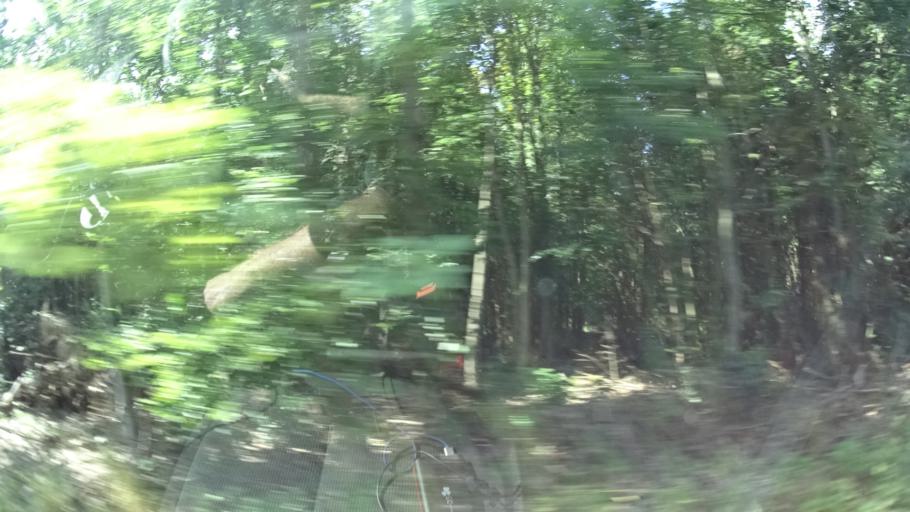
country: DE
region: Thuringia
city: Hildburghausen
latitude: 50.3893
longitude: 10.7636
